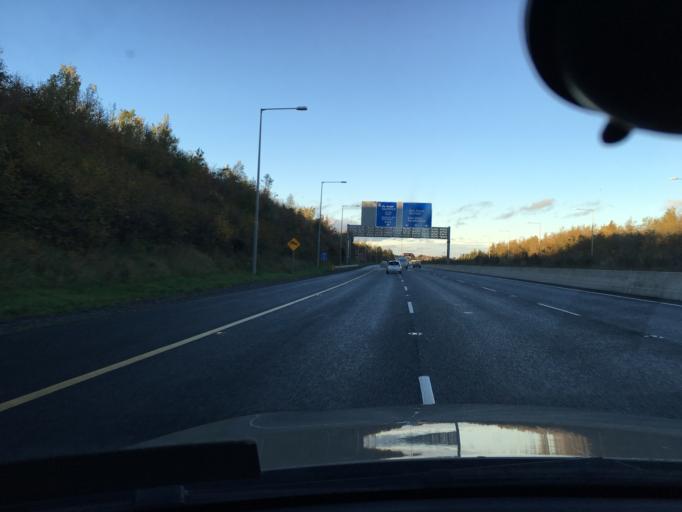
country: IE
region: Leinster
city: Kinsealy-Drinan
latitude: 53.4553
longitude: -6.2032
